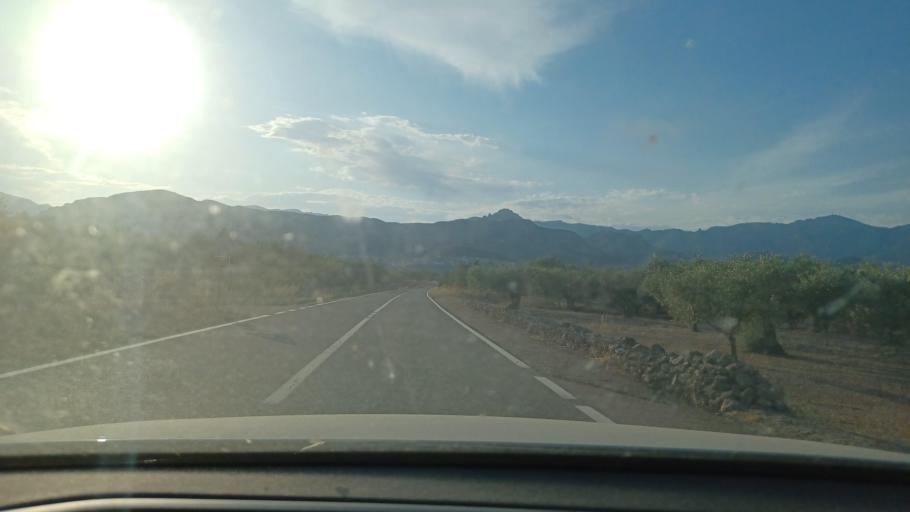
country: ES
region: Catalonia
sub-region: Provincia de Tarragona
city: Mas de Barberans
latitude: 40.7233
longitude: 0.3935
